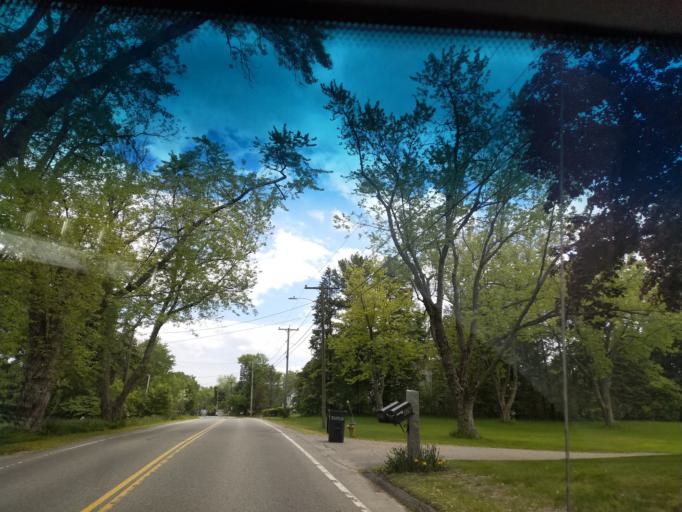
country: US
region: Maine
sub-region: Cumberland County
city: Falmouth
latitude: 43.7443
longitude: -70.2923
